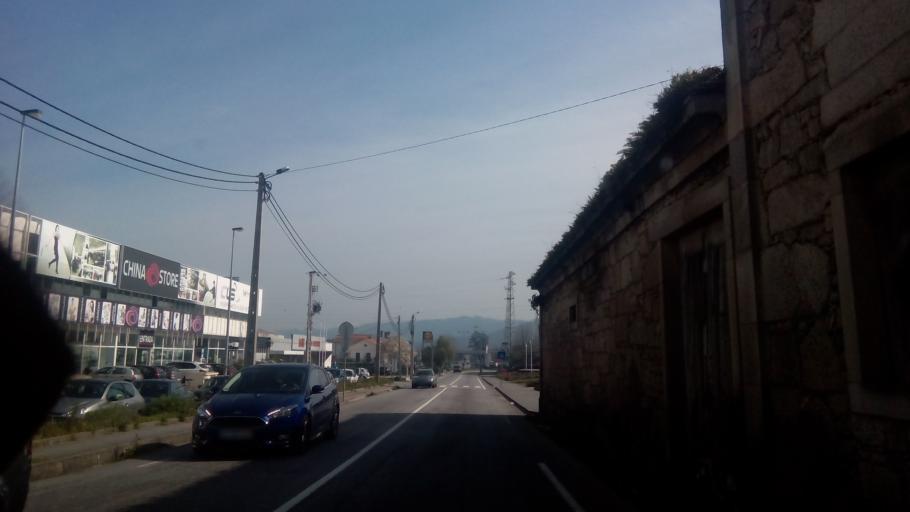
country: PT
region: Viana do Castelo
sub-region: Viana do Castelo
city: Darque
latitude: 41.6810
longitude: -8.7790
